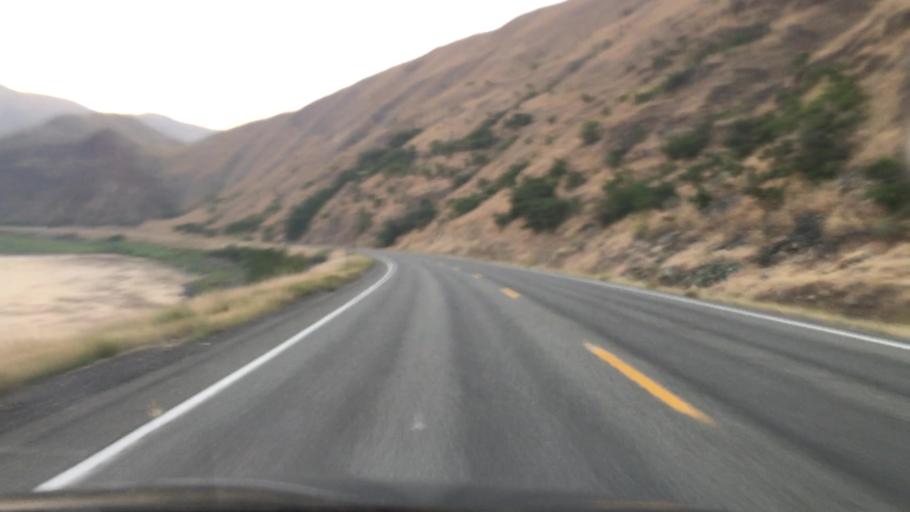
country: US
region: Idaho
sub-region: Idaho County
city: Grangeville
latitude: 45.5570
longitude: -116.2982
